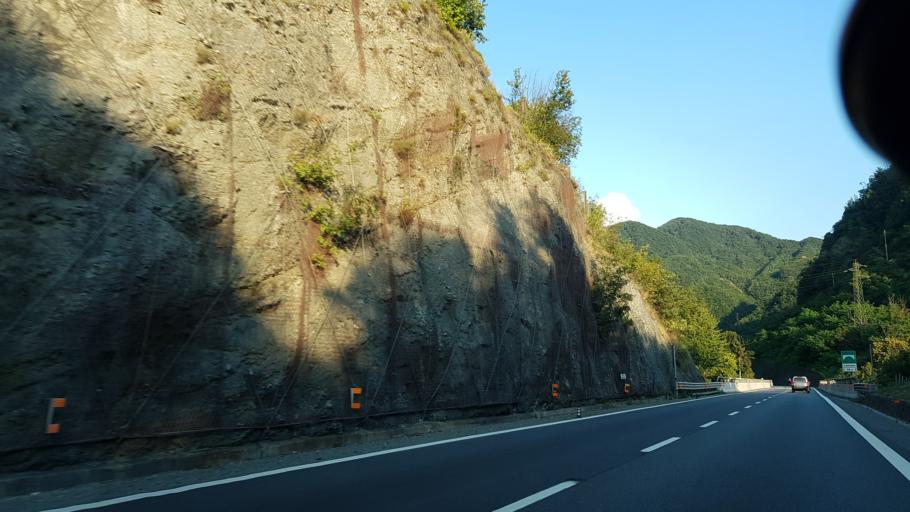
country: IT
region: Piedmont
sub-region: Provincia di Alessandria
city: Arquata Scrivia
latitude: 44.6631
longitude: 8.9134
